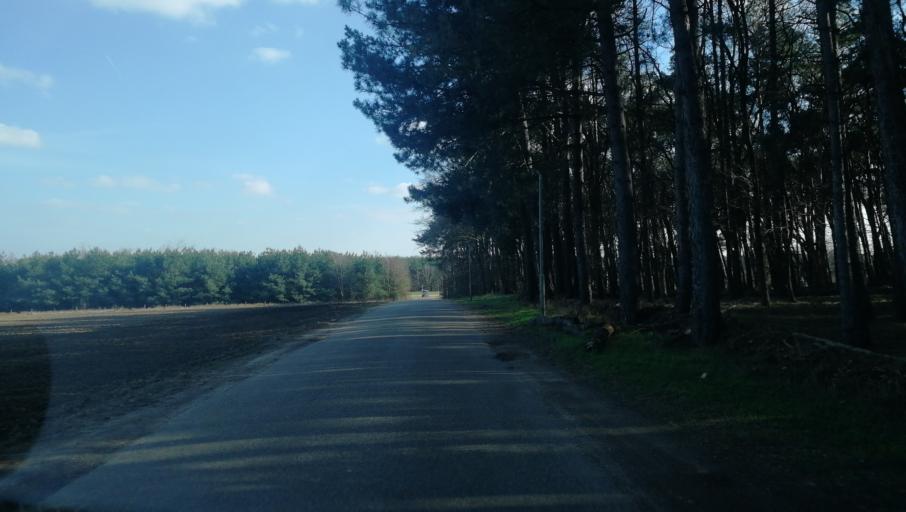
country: NL
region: Limburg
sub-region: Gemeente Venlo
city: Tegelen
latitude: 51.3870
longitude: 6.1006
